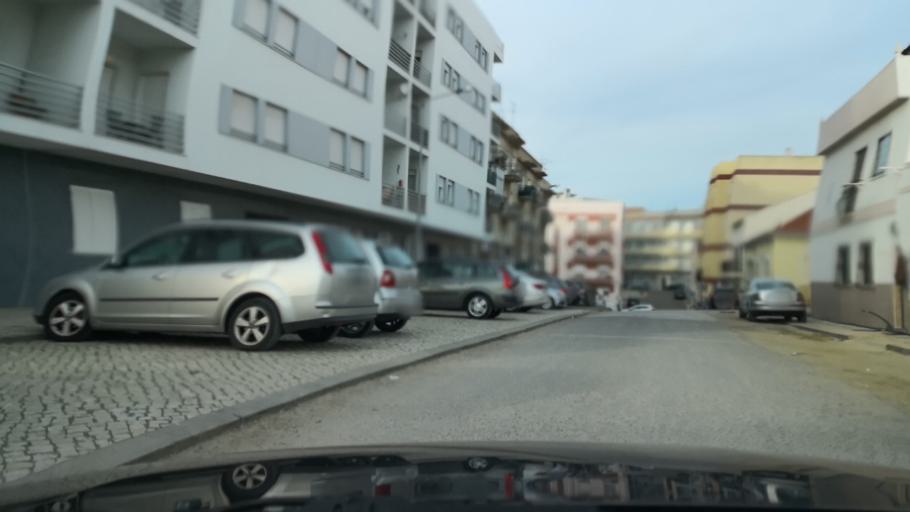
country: PT
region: Setubal
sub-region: Setubal
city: Setubal
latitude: 38.5218
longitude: -8.8809
